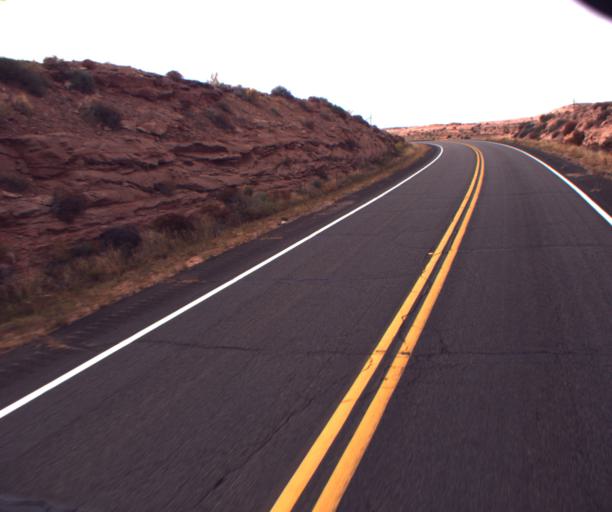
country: US
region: Arizona
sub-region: Navajo County
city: Kayenta
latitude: 36.9462
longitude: -109.7174
